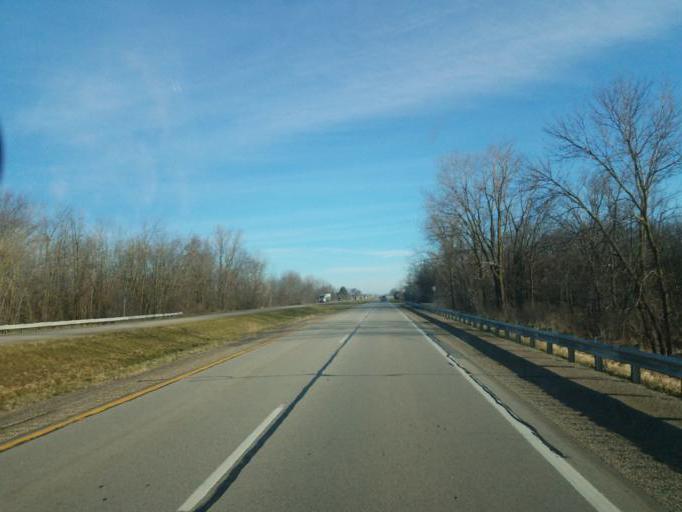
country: US
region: Michigan
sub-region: Clinton County
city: Saint Johns
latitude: 43.1457
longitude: -84.5632
